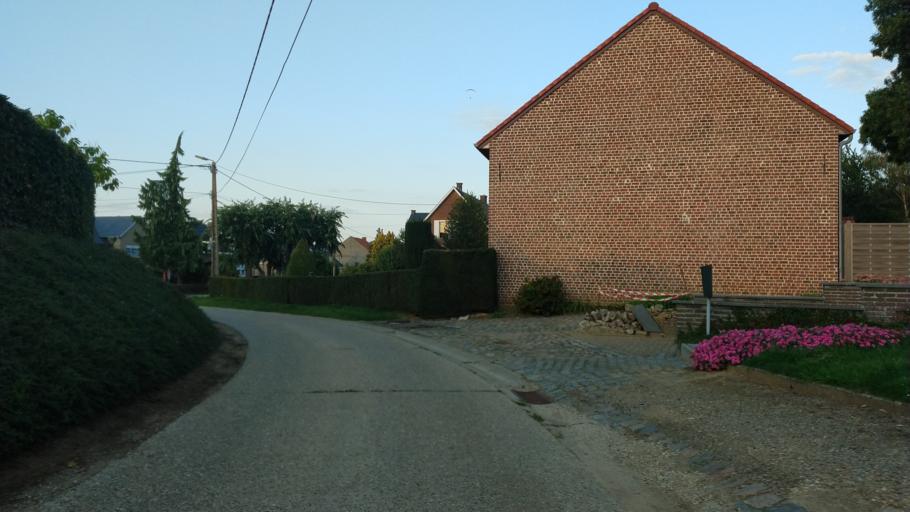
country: BE
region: Flanders
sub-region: Provincie Vlaams-Brabant
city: Lubbeek
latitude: 50.8911
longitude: 4.8135
